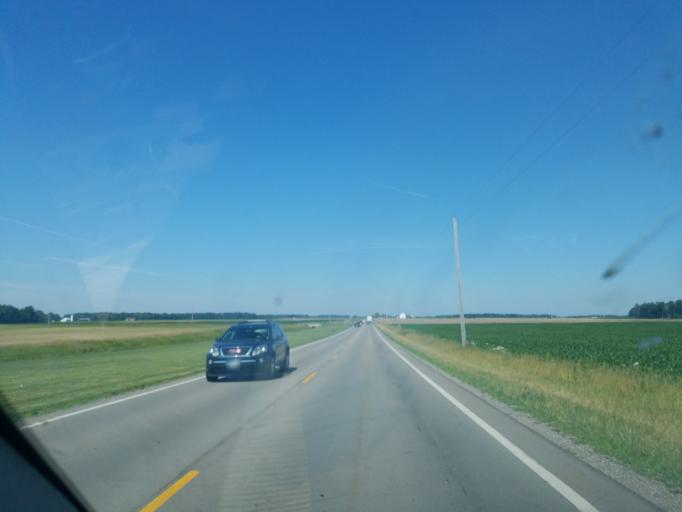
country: US
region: Ohio
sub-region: Logan County
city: Lakeview
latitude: 40.4393
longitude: -83.9618
